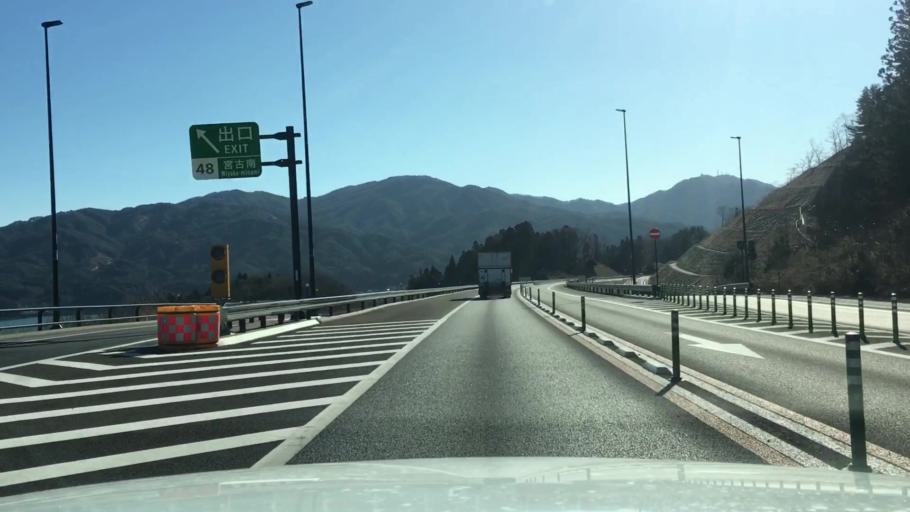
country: JP
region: Iwate
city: Miyako
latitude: 39.5982
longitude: 141.9375
